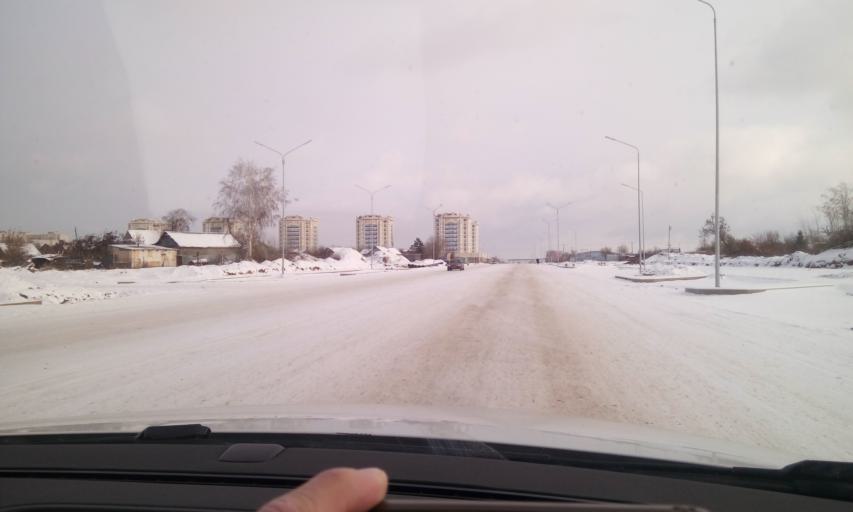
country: KZ
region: Astana Qalasy
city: Astana
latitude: 51.1203
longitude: 71.4967
